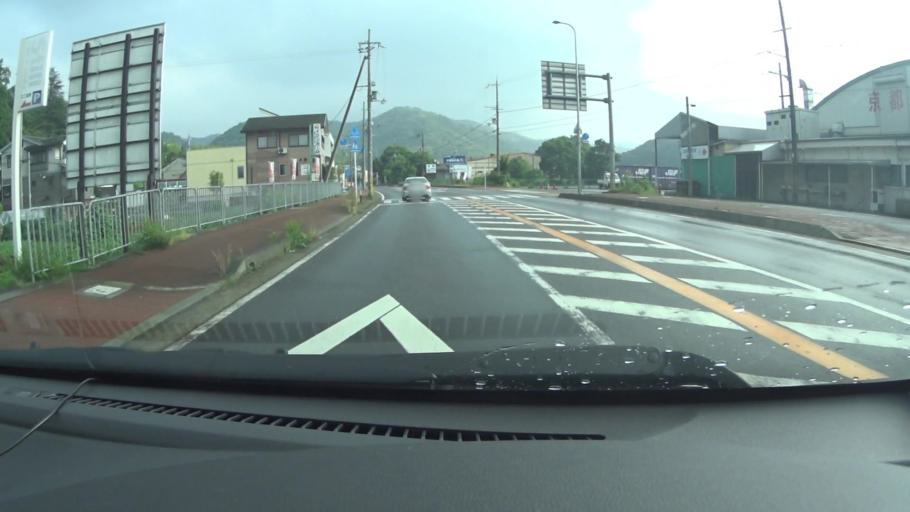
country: JP
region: Kyoto
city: Ayabe
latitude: 35.2983
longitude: 135.2671
